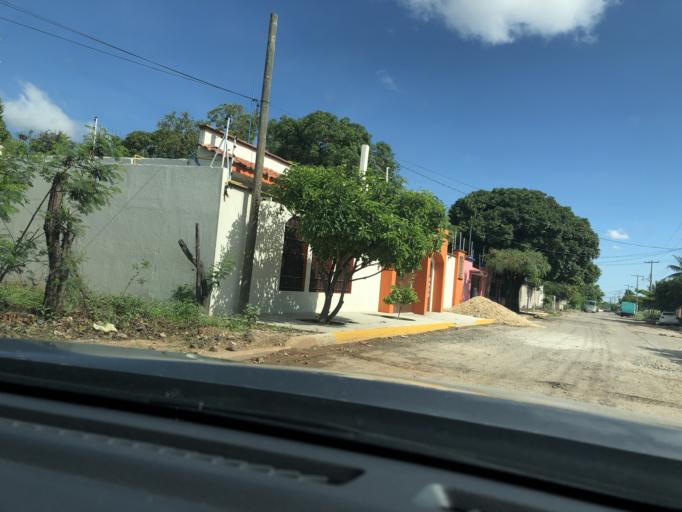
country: MX
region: Oaxaca
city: San Jeronimo Ixtepec
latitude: 16.5573
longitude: -95.1037
